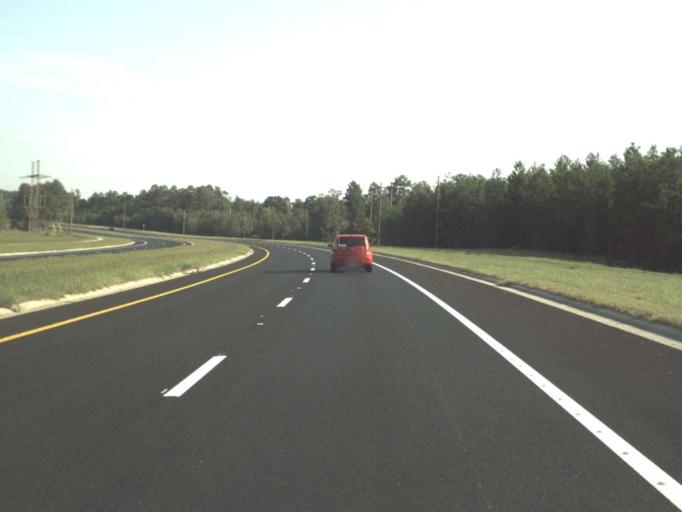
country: US
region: Florida
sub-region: Holmes County
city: Bonifay
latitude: 30.5659
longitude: -85.8078
